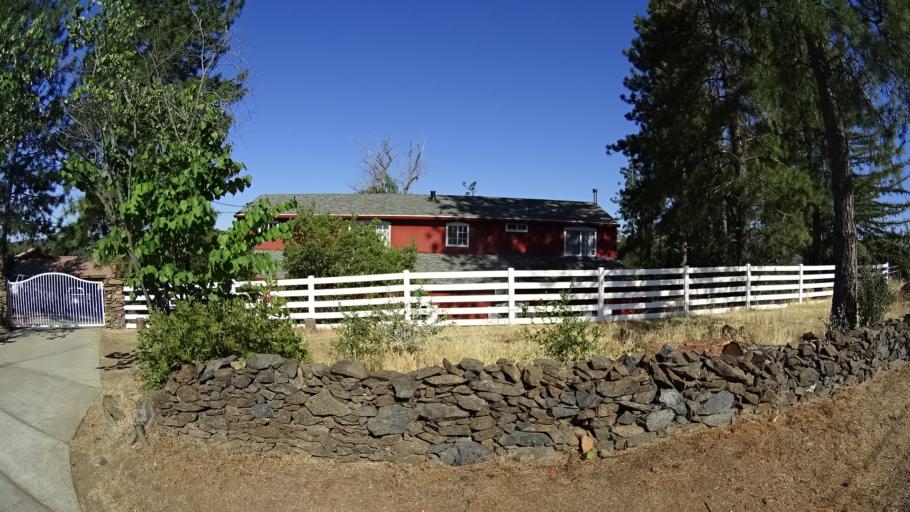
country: US
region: California
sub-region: Calaveras County
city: Murphys
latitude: 38.0772
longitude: -120.4616
